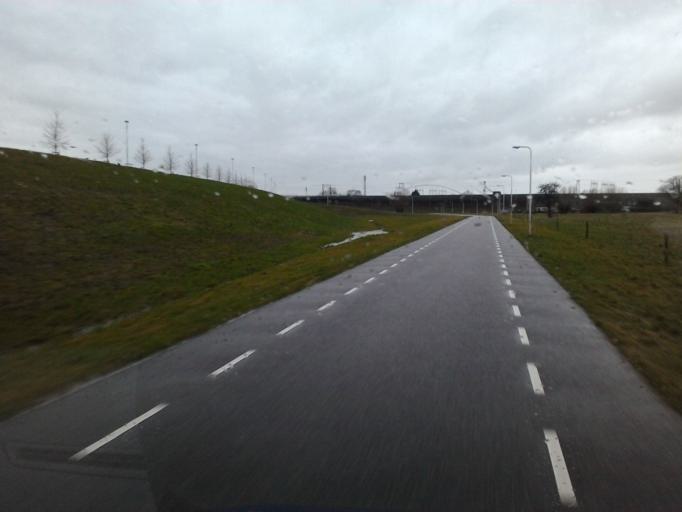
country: NL
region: Gelderland
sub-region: Gemeente Nijmegen
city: Nijmegen
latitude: 51.8576
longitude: 5.8649
